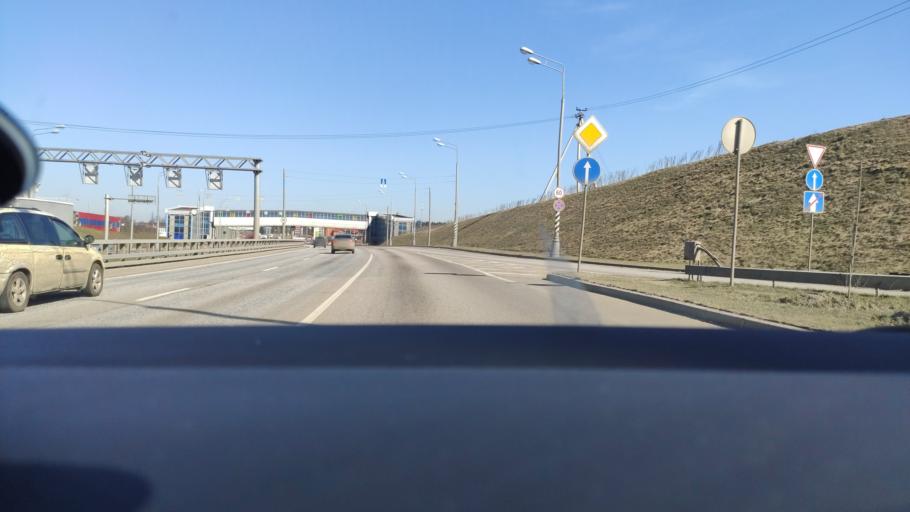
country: RU
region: Moskovskaya
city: Filimonki
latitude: 55.5210
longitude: 37.3817
